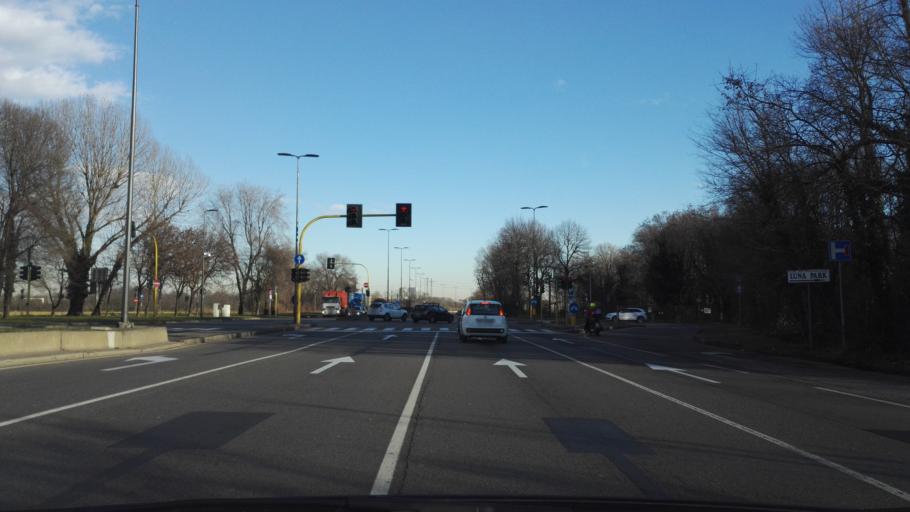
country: IT
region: Lombardy
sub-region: Citta metropolitana di Milano
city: Figino
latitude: 45.4879
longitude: 9.0736
